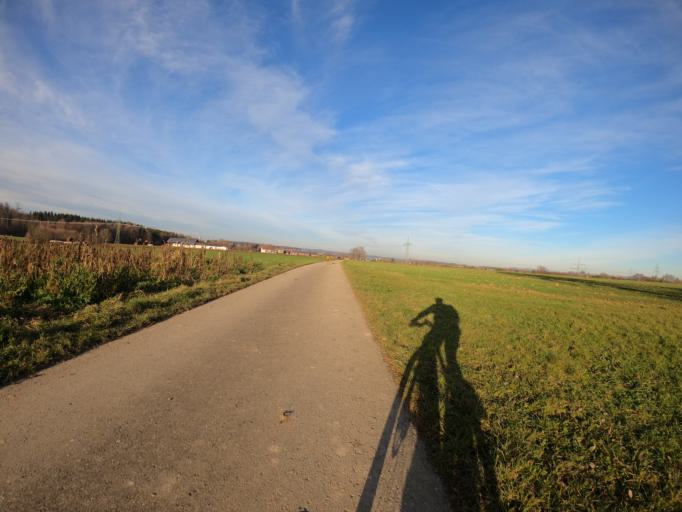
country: DE
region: Baden-Wuerttemberg
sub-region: Regierungsbezirk Stuttgart
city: Albershausen
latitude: 48.6741
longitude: 9.5541
